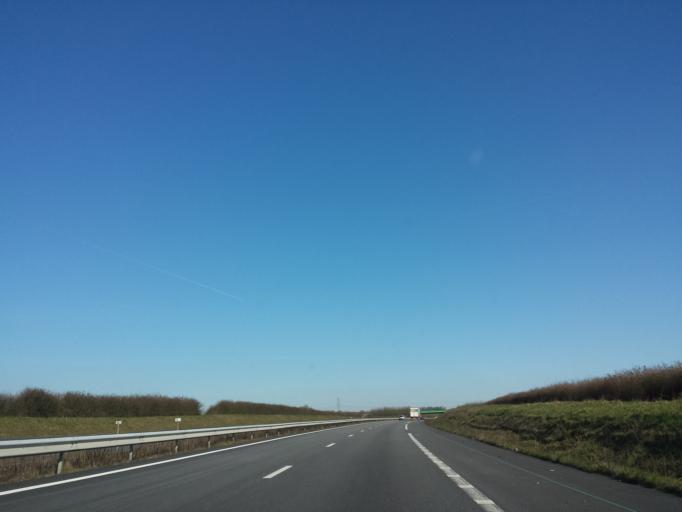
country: FR
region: Picardie
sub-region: Departement de l'Oise
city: Saint-Crepin-Ibouvillers
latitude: 49.2981
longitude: 2.0725
